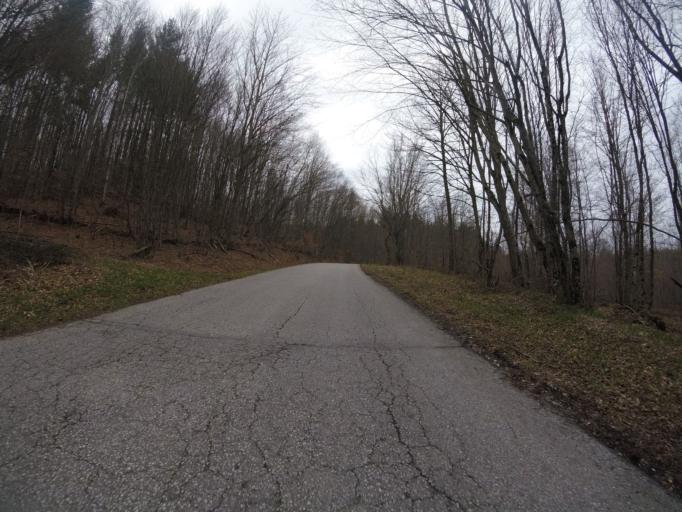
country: HR
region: Zagrebacka
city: Lukavec
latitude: 45.5578
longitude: 15.9812
